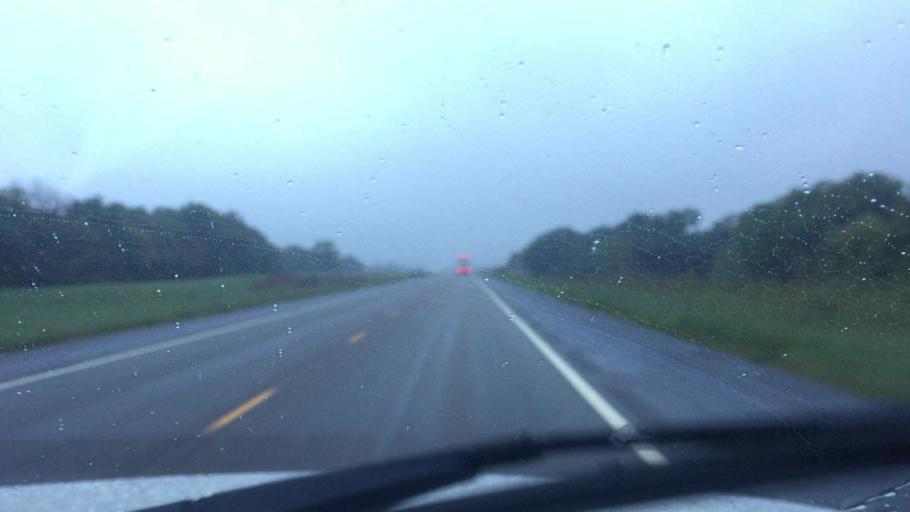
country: US
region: Kansas
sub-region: Montgomery County
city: Cherryvale
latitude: 37.4118
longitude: -95.4988
